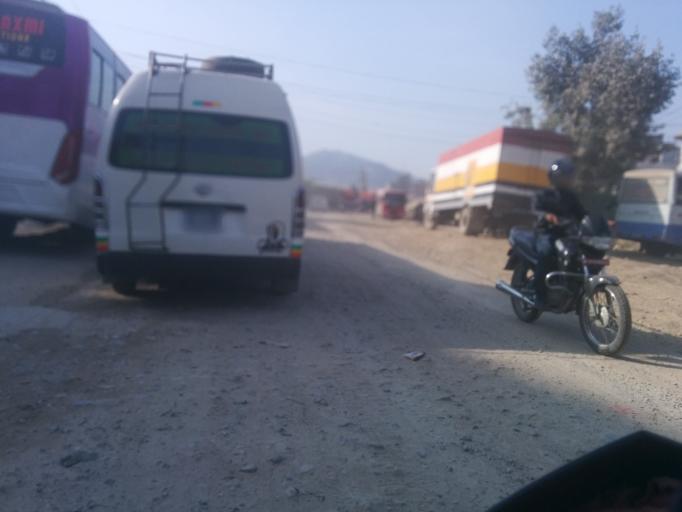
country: NP
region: Central Region
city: Kirtipur
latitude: 27.6886
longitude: 85.2852
